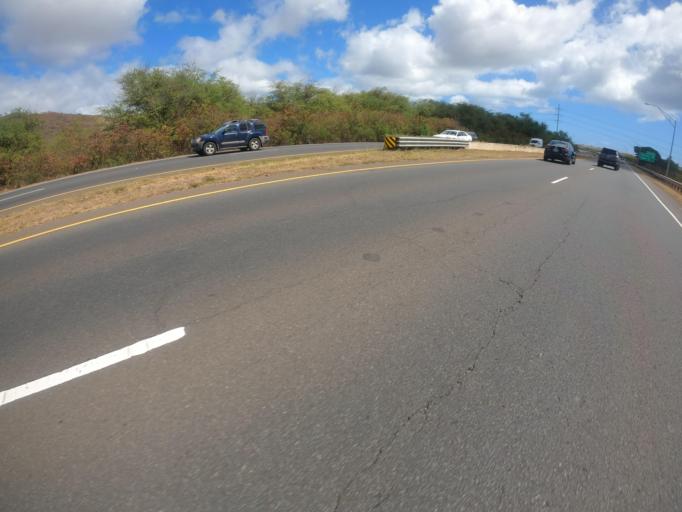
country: US
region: Hawaii
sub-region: Honolulu County
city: Makakilo City
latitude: 21.3348
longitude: -158.0951
